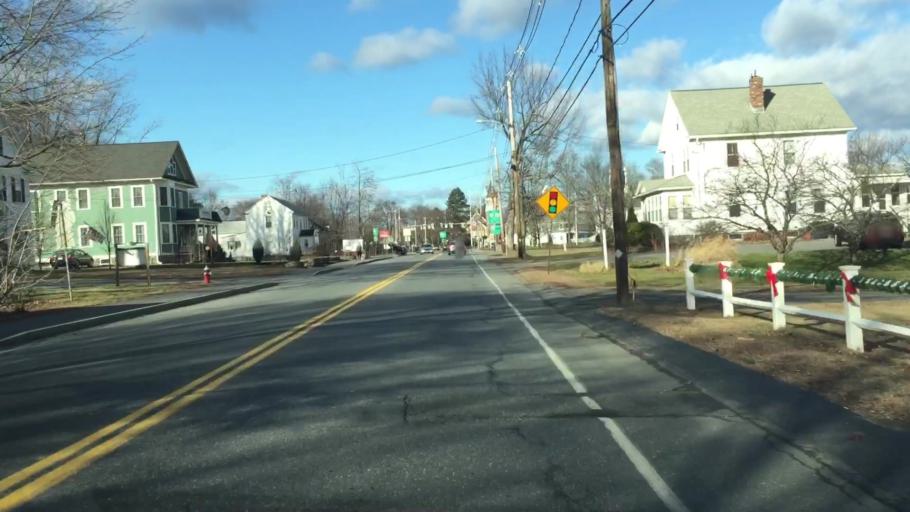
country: US
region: Massachusetts
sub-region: Worcester County
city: West Boylston
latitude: 42.3610
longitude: -71.7808
